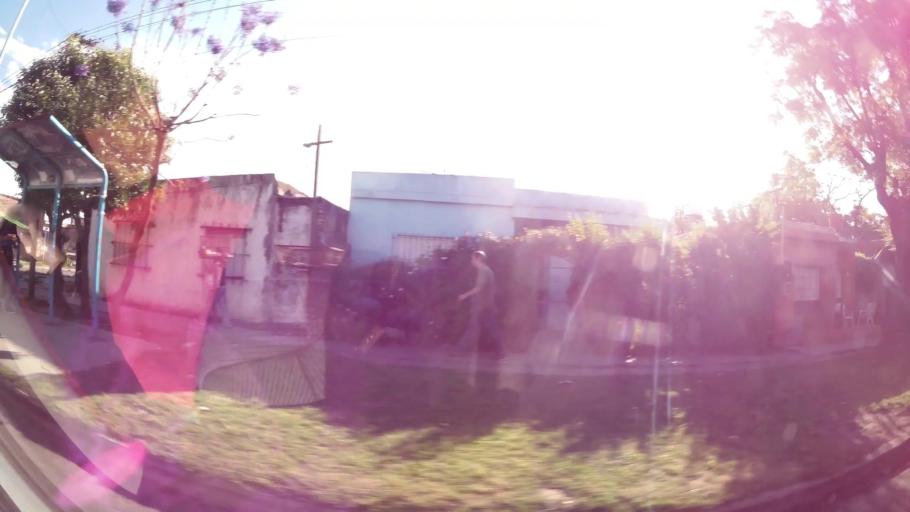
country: AR
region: Buenos Aires
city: Hurlingham
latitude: -34.5034
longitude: -58.7245
